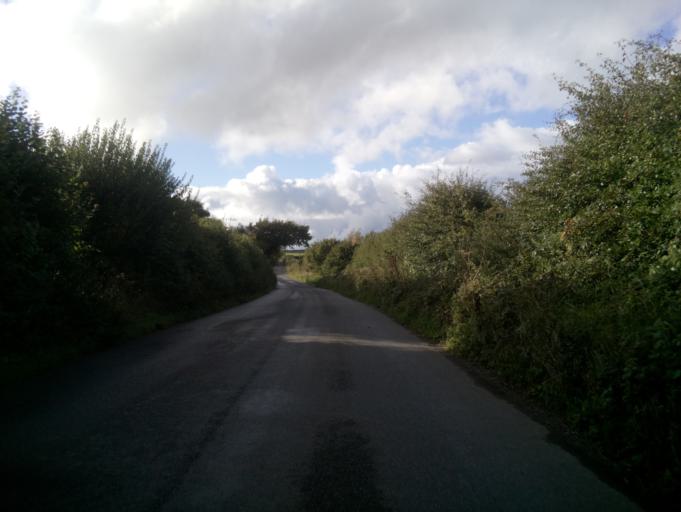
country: GB
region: England
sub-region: Devon
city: South Brent
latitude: 50.3895
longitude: -3.7701
